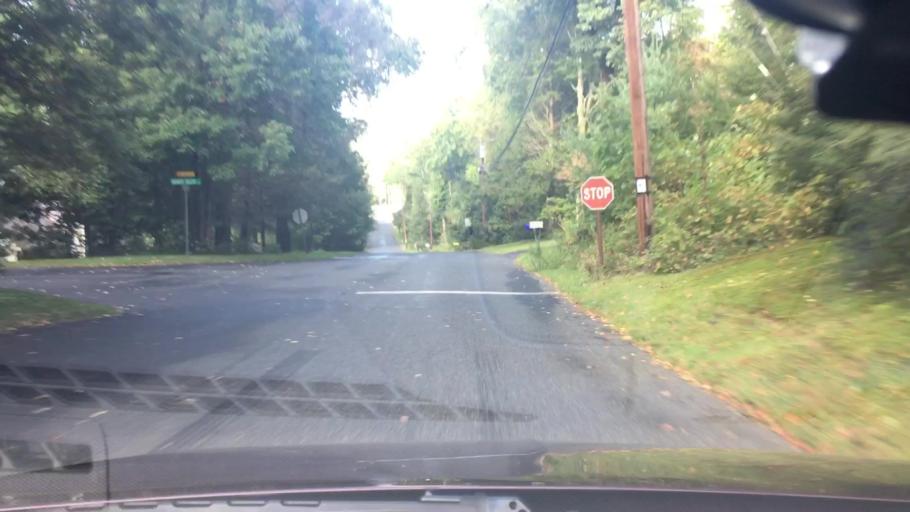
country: US
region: Connecticut
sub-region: Tolland County
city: Somers
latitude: 41.9760
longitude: -72.4130
